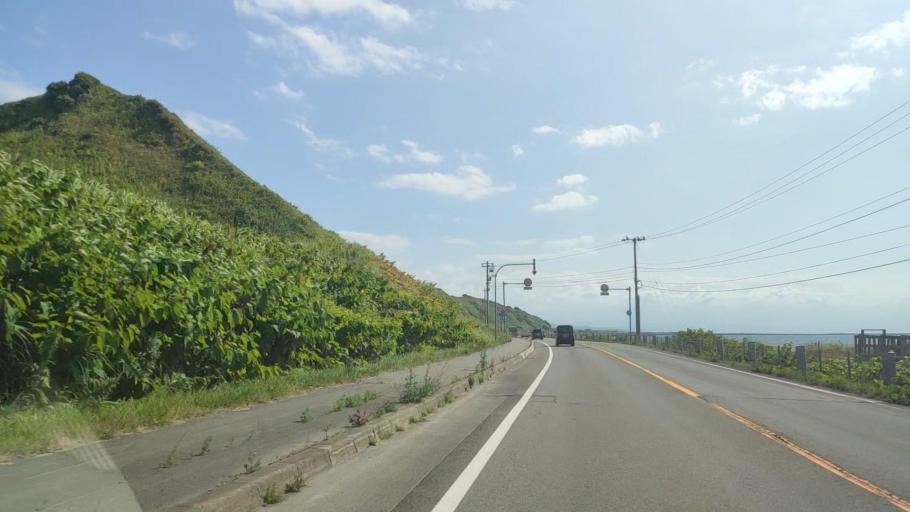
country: JP
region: Hokkaido
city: Rumoi
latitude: 43.9946
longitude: 141.6517
